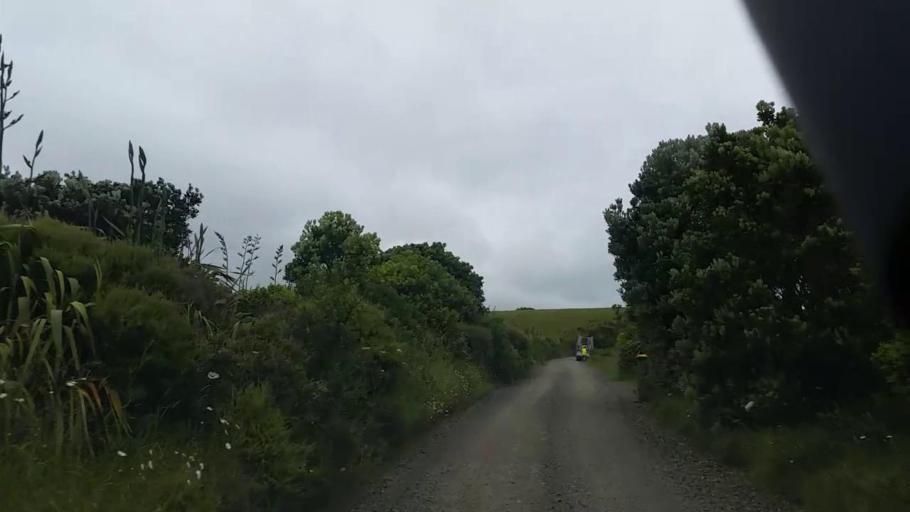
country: NZ
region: Auckland
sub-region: Auckland
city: Muriwai Beach
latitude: -36.9284
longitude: 174.4605
